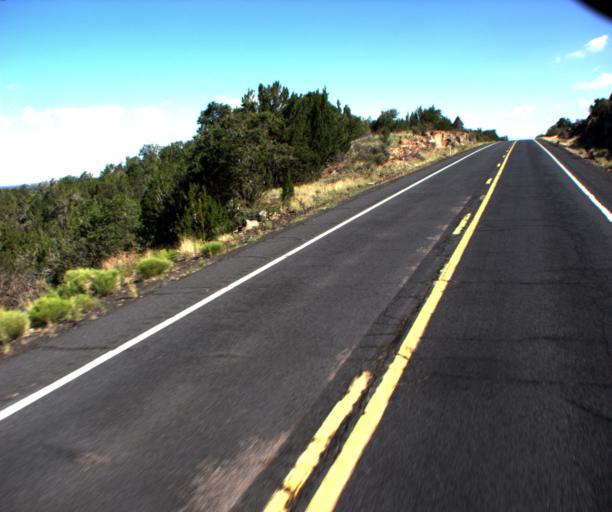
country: US
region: Arizona
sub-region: Coconino County
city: Williams
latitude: 35.4285
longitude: -112.1709
